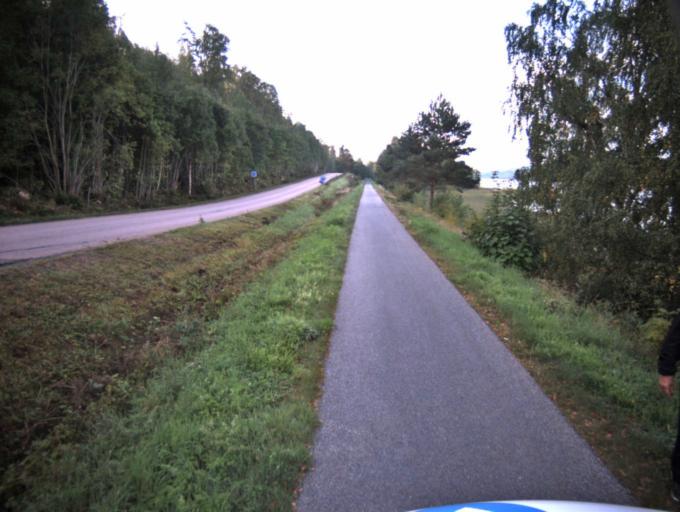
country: SE
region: Vaestra Goetaland
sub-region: Ulricehamns Kommun
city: Ulricehamn
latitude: 57.7509
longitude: 13.3943
